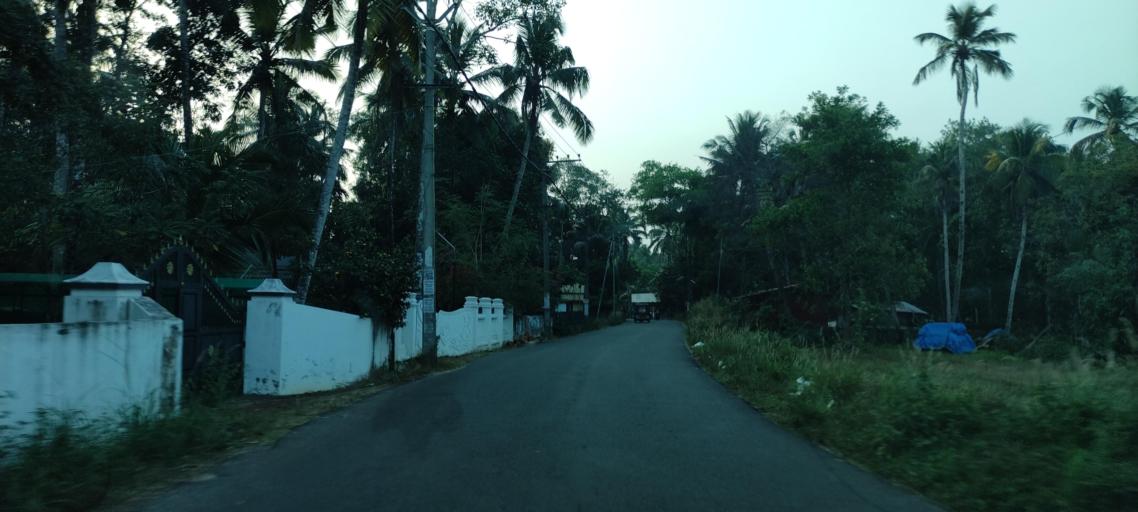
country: IN
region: Kerala
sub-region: Alappuzha
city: Kayankulam
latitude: 9.1372
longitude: 76.5188
